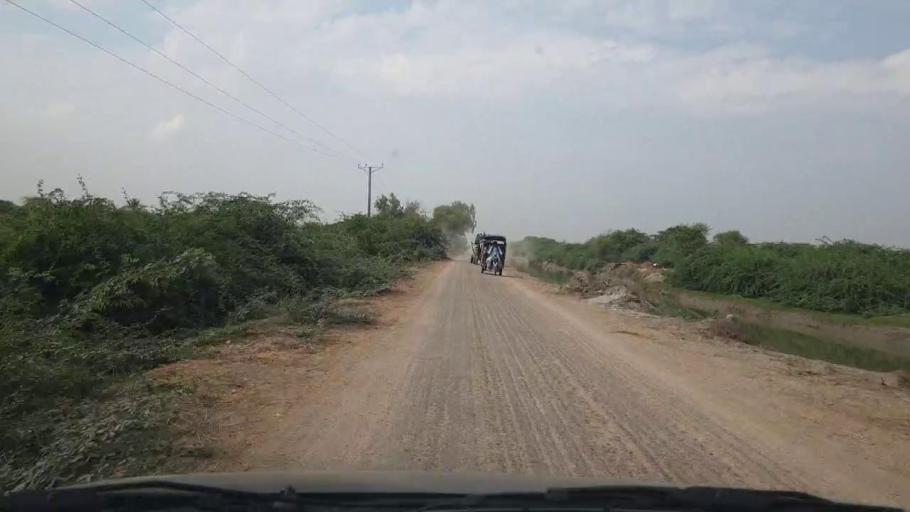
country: PK
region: Sindh
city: Kario
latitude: 24.6299
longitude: 68.5726
